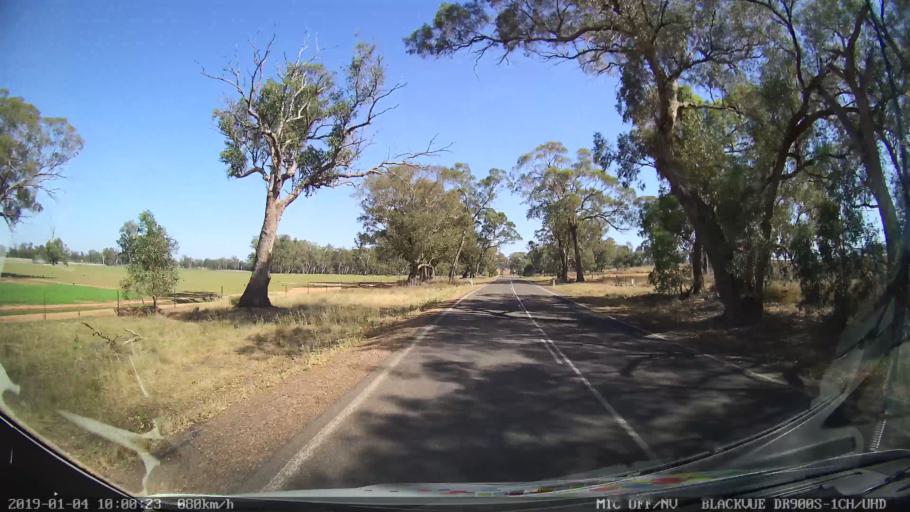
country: AU
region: New South Wales
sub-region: Cabonne
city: Canowindra
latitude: -33.4983
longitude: 148.3793
